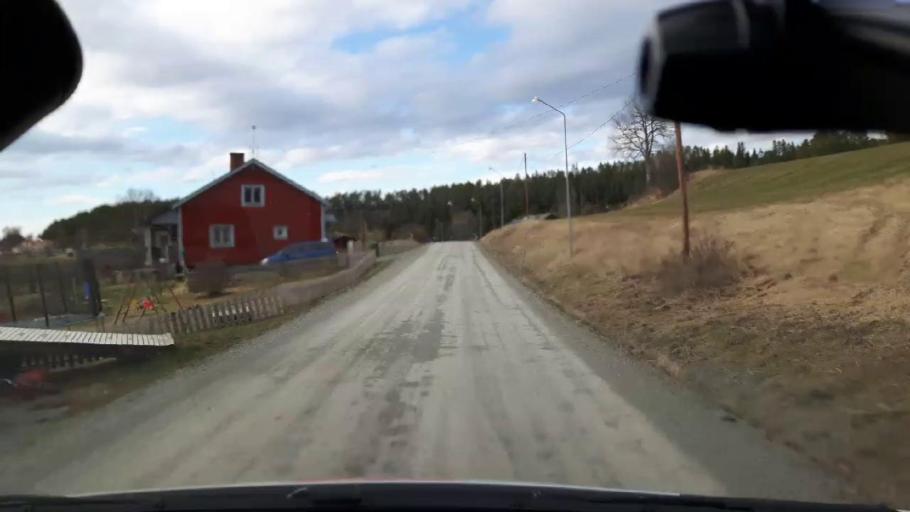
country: SE
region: Jaemtland
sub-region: OEstersunds Kommun
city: Brunflo
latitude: 62.9506
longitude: 14.6585
